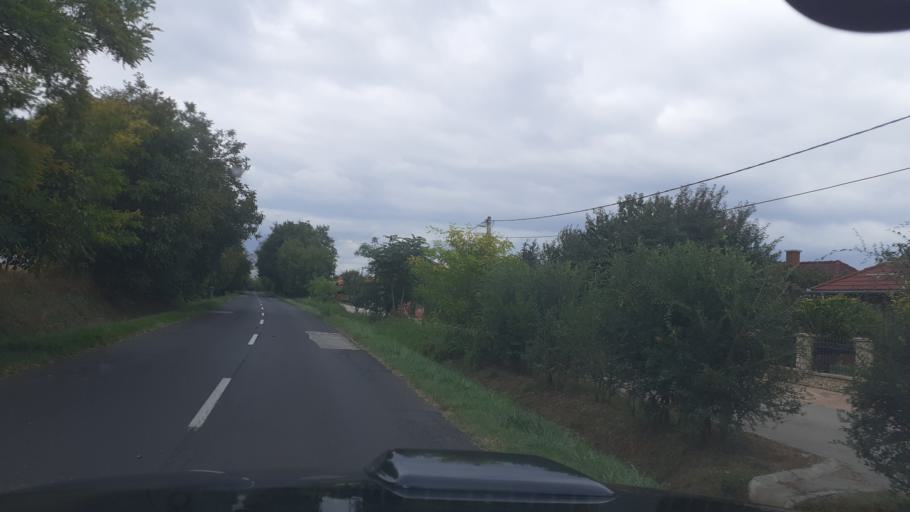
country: HU
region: Fejer
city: Racalmas
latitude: 47.0330
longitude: 18.9364
